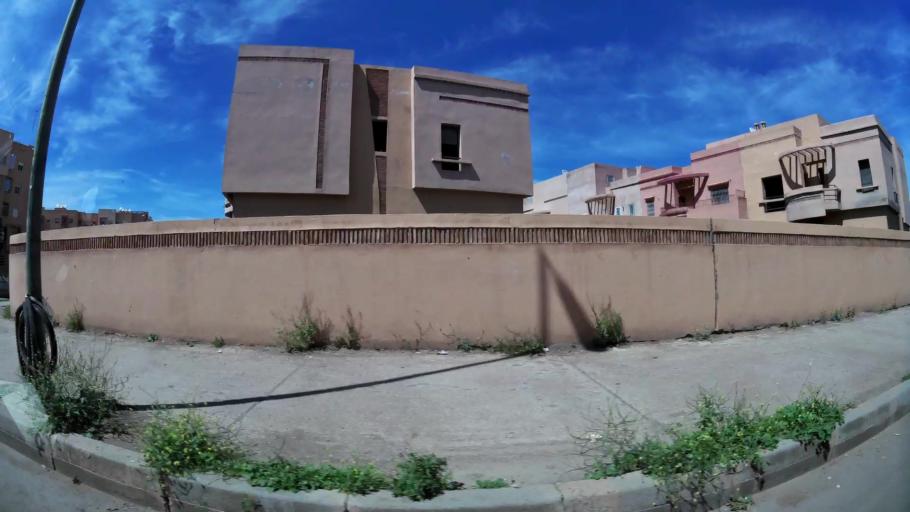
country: MA
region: Marrakech-Tensift-Al Haouz
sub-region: Marrakech
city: Marrakesh
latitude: 31.6459
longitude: -8.0715
